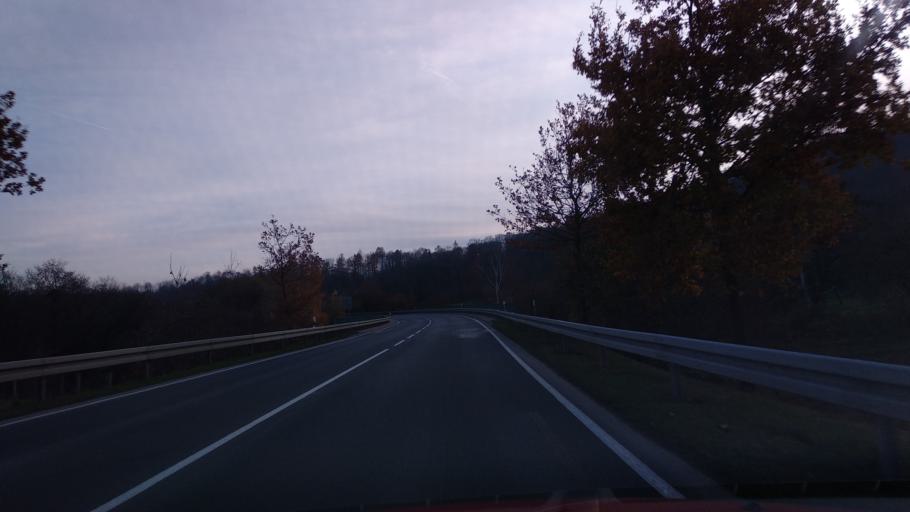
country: DE
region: Lower Saxony
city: Furstenberg
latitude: 51.7095
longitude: 9.3765
